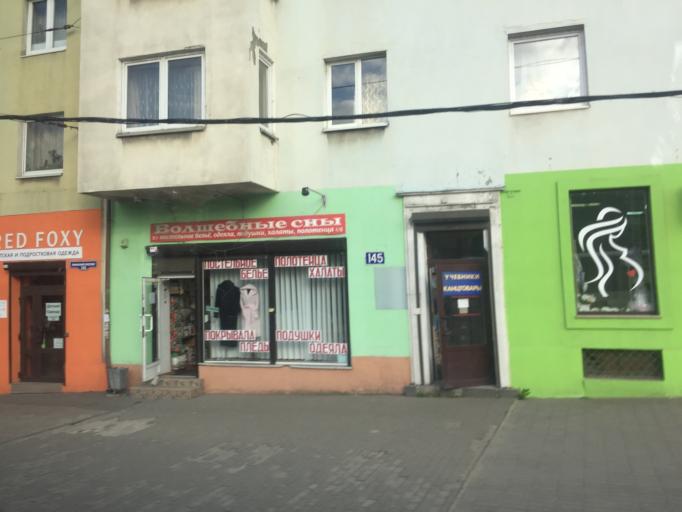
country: RU
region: Kaliningrad
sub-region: Gorod Kaliningrad
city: Kaliningrad
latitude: 54.6976
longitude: 20.5029
